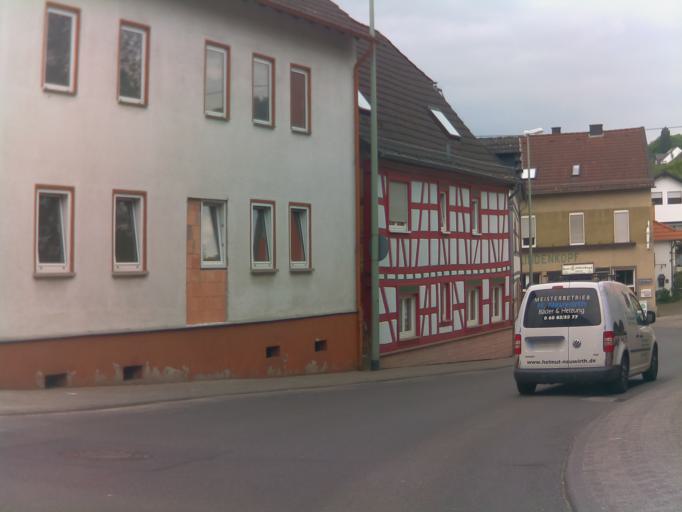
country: DE
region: Hesse
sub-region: Regierungsbezirk Darmstadt
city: Niedernhausen
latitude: 50.1704
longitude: 8.3375
